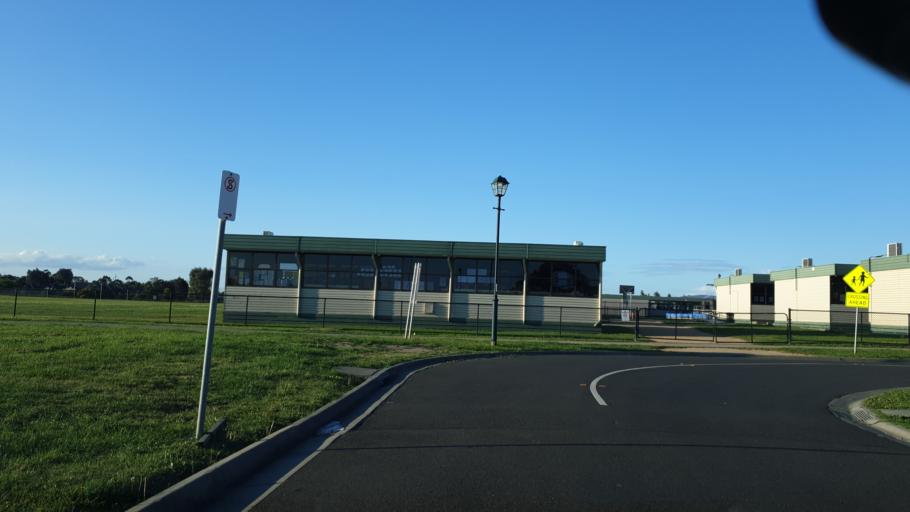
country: AU
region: Victoria
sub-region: Casey
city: Cranbourne East
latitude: -38.1065
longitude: 145.3035
